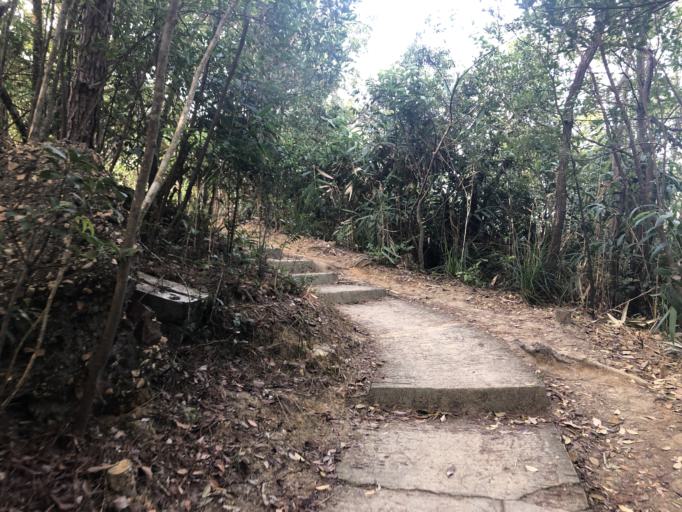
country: HK
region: Wanchai
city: Wan Chai
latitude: 22.2772
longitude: 114.2125
